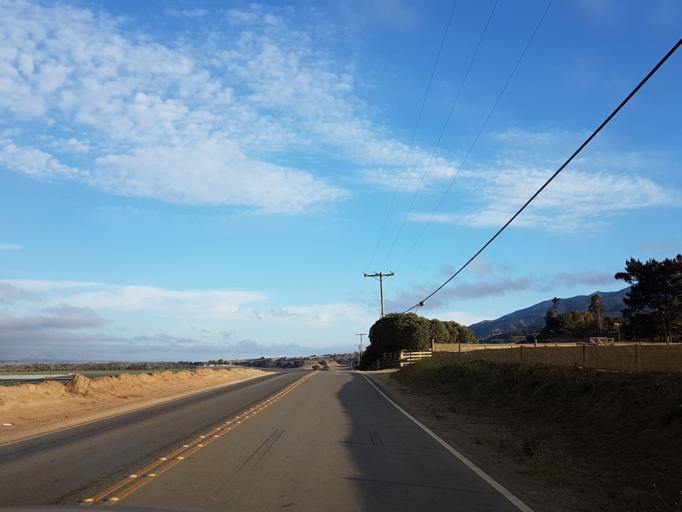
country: US
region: California
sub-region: Monterey County
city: Chualar
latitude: 36.5879
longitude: -121.6032
